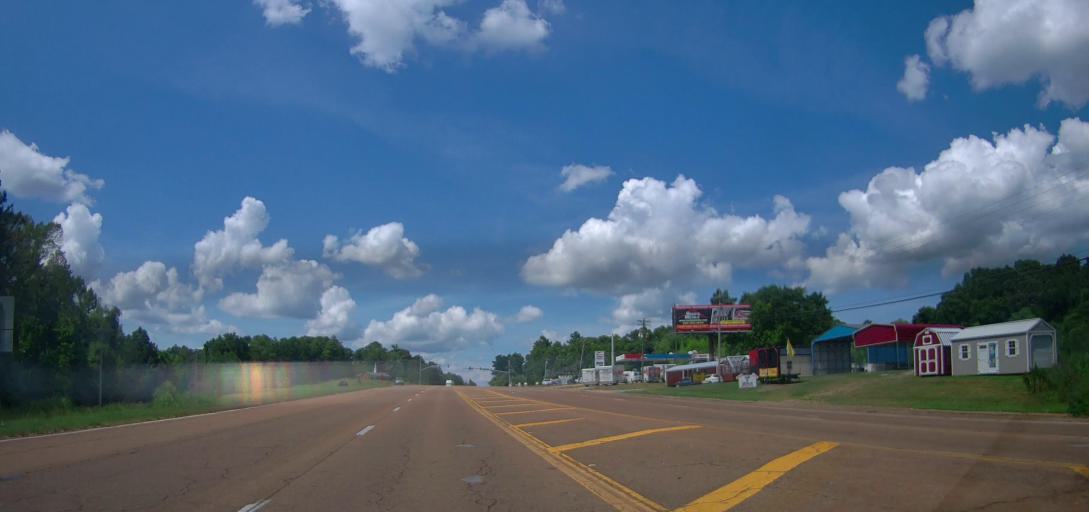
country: US
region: Mississippi
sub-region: Lowndes County
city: Columbus
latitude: 33.5610
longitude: -88.4330
